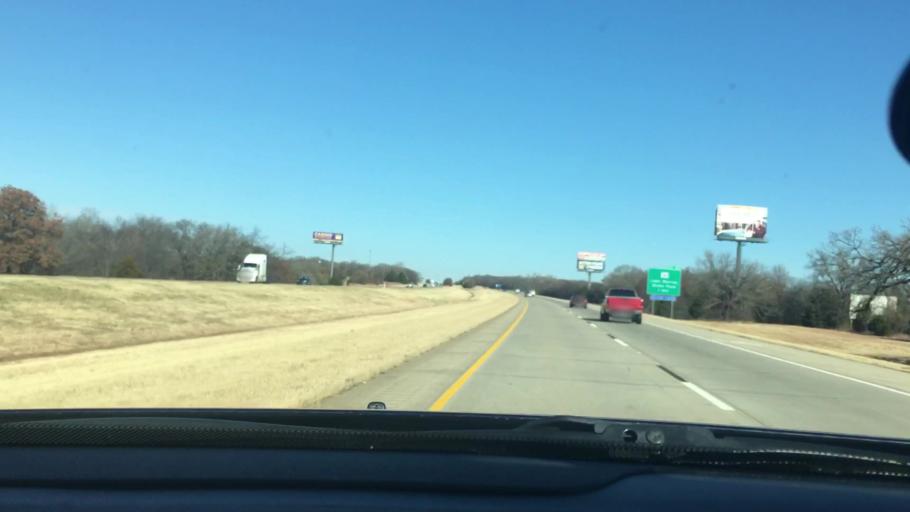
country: US
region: Oklahoma
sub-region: Love County
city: Marietta
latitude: 34.0508
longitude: -97.1487
